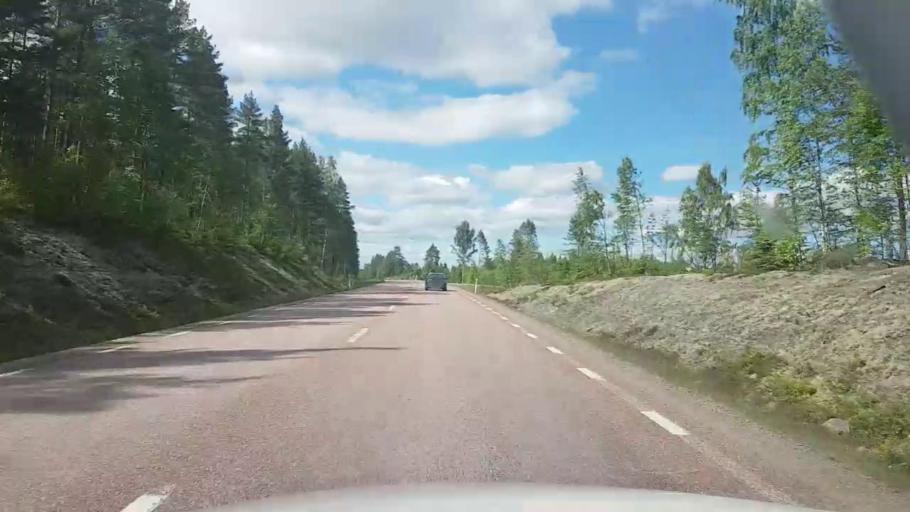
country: SE
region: Gaevleborg
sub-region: Ljusdals Kommun
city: Jaervsoe
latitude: 61.7691
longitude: 16.1562
